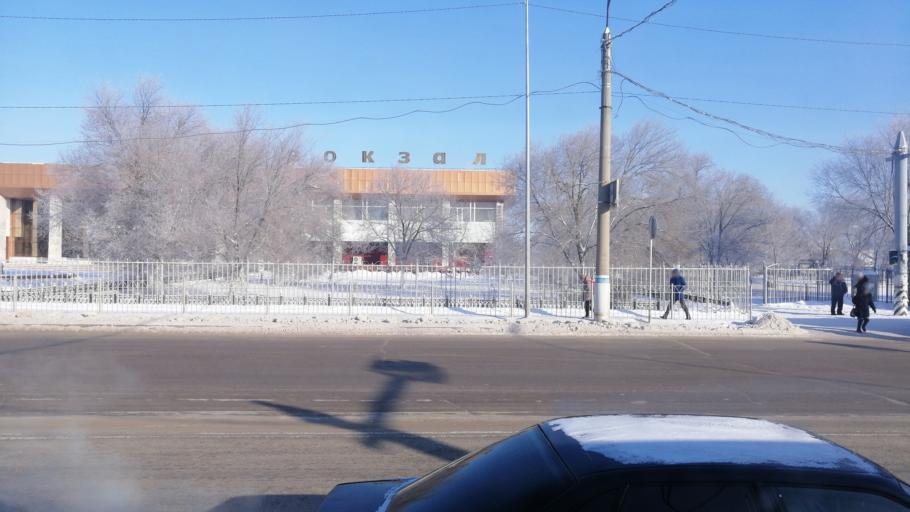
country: KZ
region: Aqtoebe
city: Aqtobe
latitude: 50.2928
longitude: 57.1989
